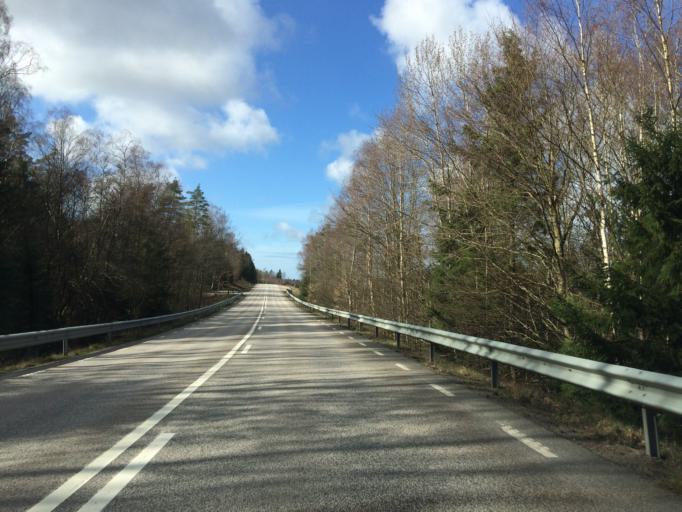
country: SE
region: Halland
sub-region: Laholms Kommun
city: Knared
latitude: 56.4979
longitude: 13.3766
